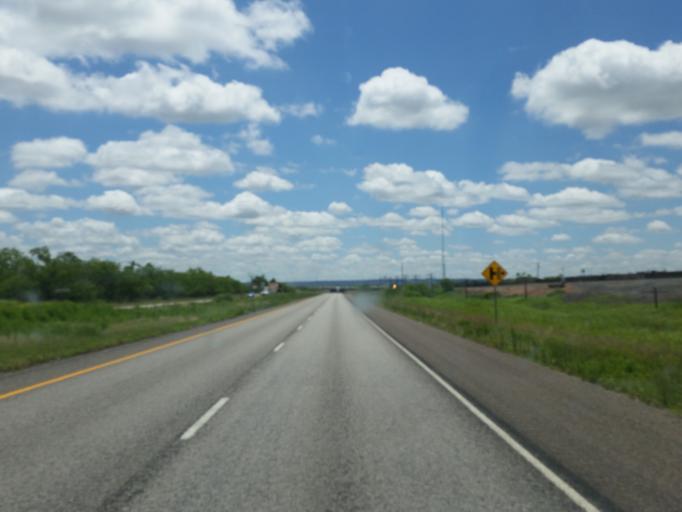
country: US
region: Texas
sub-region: Garza County
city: Post
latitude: 33.0461
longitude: -101.2056
